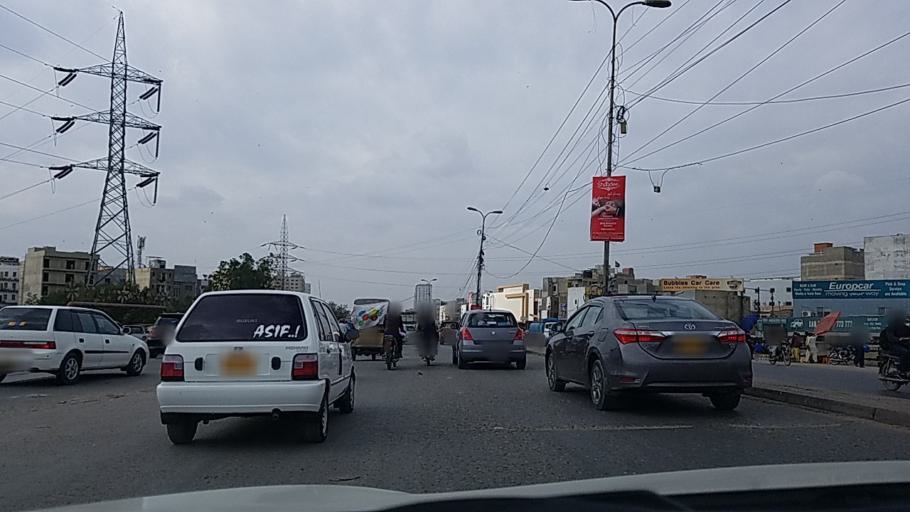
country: PK
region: Sindh
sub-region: Karachi District
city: Karachi
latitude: 24.8323
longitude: 67.0764
